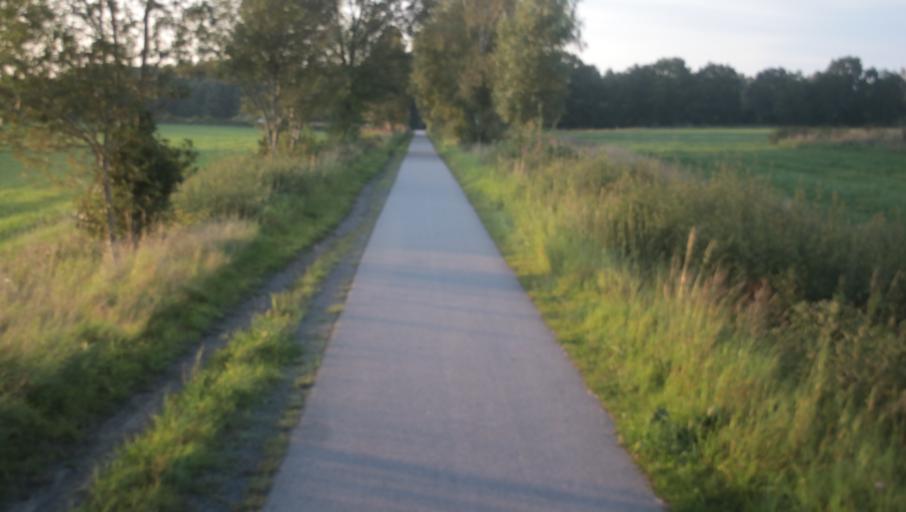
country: SE
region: Blekinge
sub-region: Karlshamns Kommun
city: Karlshamn
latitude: 56.2165
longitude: 14.8239
